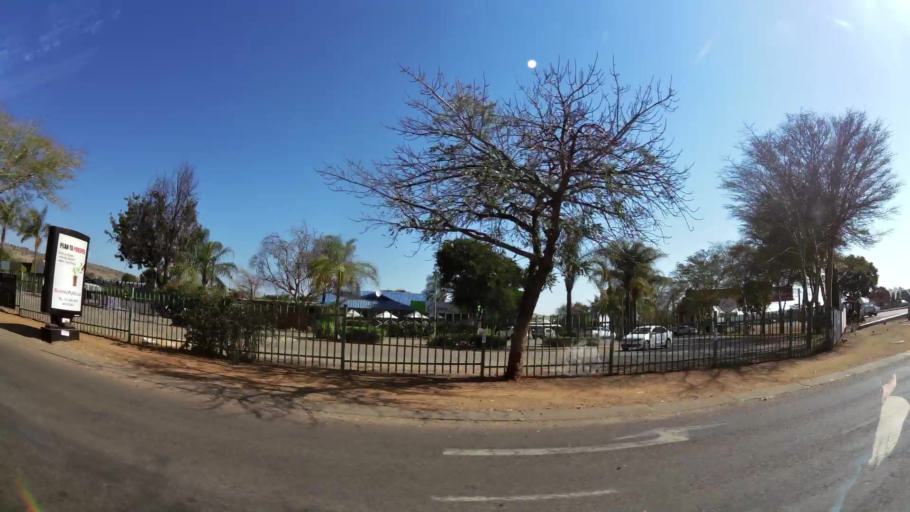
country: ZA
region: Gauteng
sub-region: City of Tshwane Metropolitan Municipality
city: Pretoria
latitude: -25.6832
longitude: 28.2712
